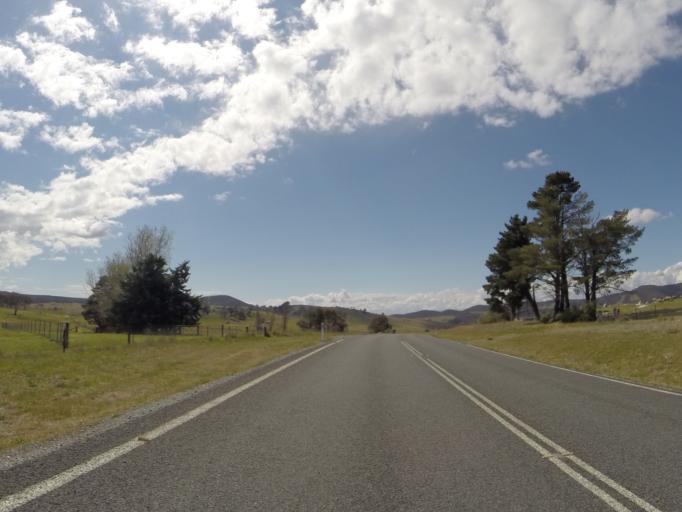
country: AU
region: Australian Capital Territory
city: Macarthur
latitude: -35.4116
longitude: 148.9460
